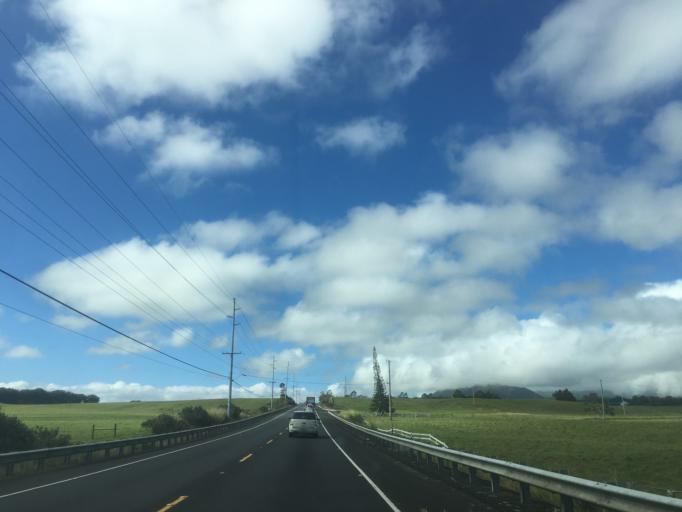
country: US
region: Hawaii
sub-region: Hawaii County
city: Waimea
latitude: 20.0484
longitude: -155.5759
